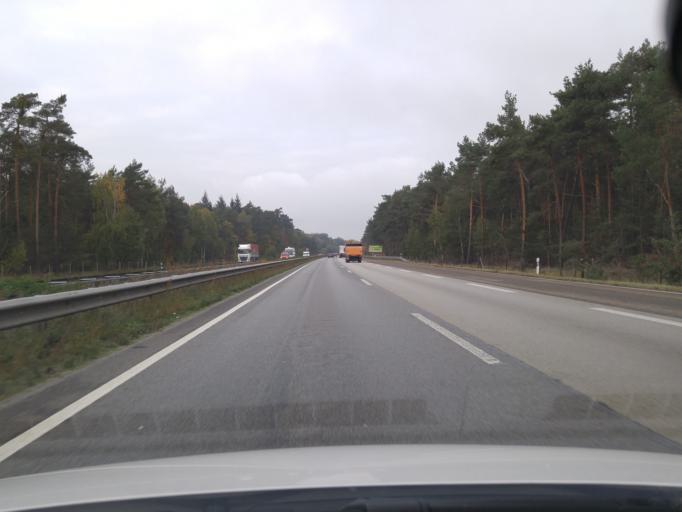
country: DE
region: Rheinland-Pfalz
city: Schifferstadt
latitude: 49.3565
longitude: 8.3804
